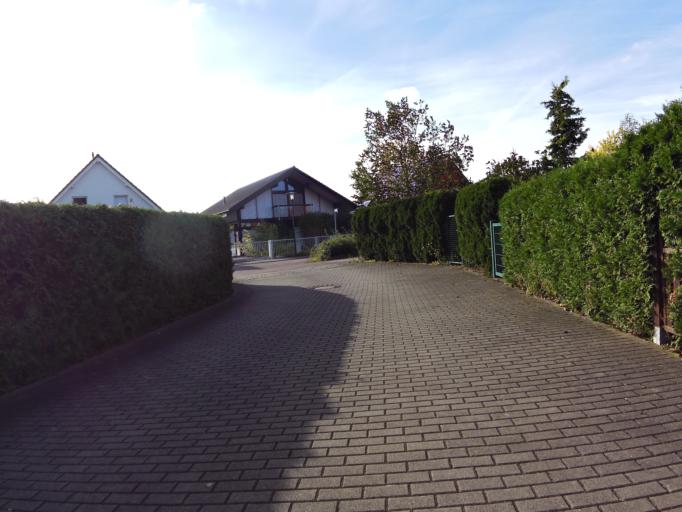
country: DE
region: Saxony
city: Markkleeberg
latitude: 51.3047
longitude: 12.4338
